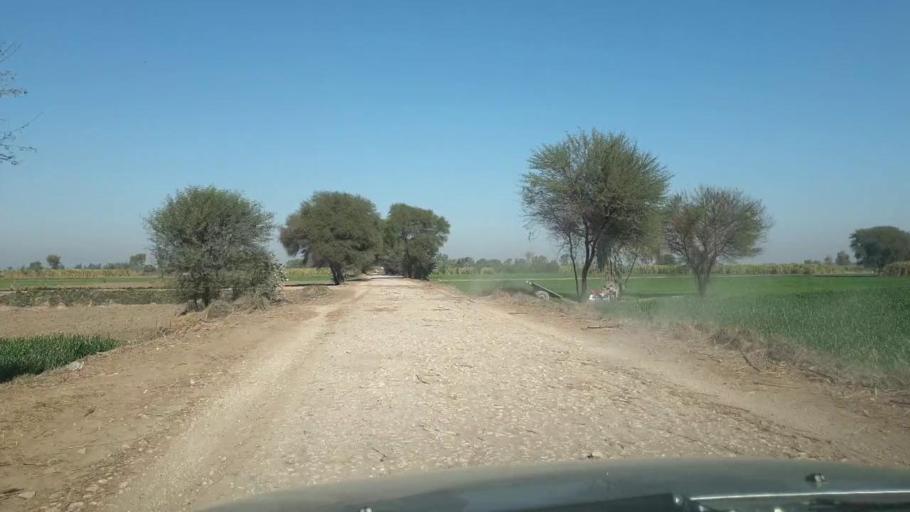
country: PK
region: Sindh
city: Ghotki
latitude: 28.0911
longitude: 69.3434
